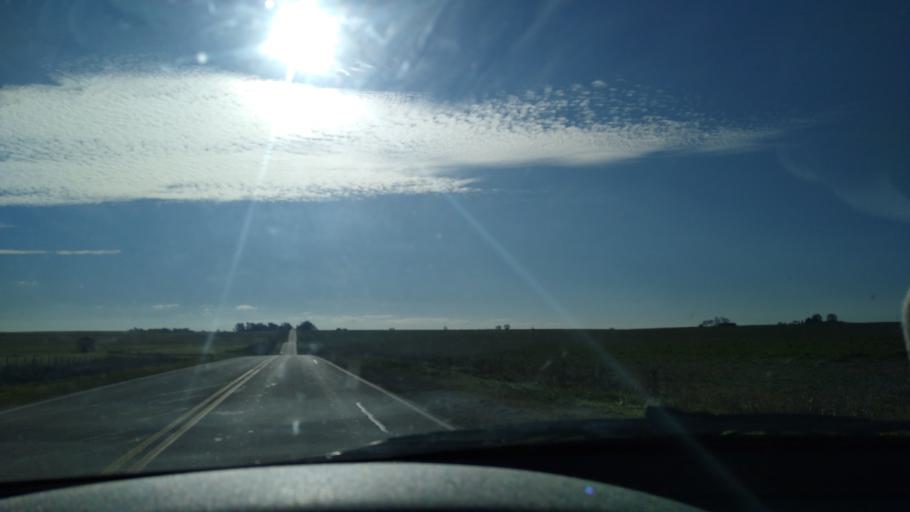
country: AR
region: Entre Rios
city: Aranguren
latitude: -32.3439
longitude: -60.3710
